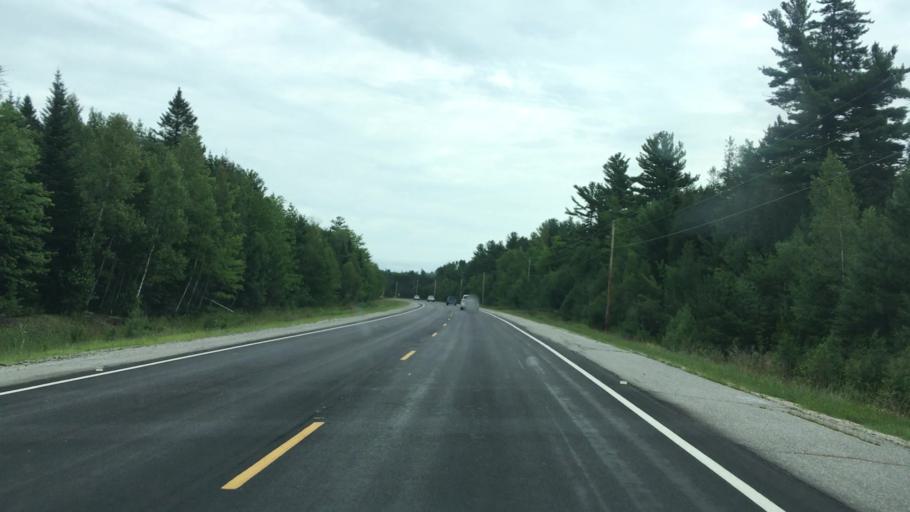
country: US
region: Maine
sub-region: Washington County
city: Addison
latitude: 44.9405
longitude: -67.7185
